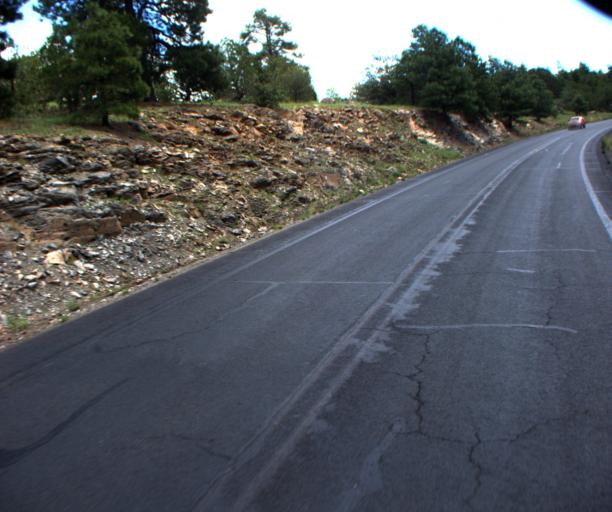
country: US
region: Arizona
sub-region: Gila County
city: Pine
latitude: 34.5170
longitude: -111.4996
